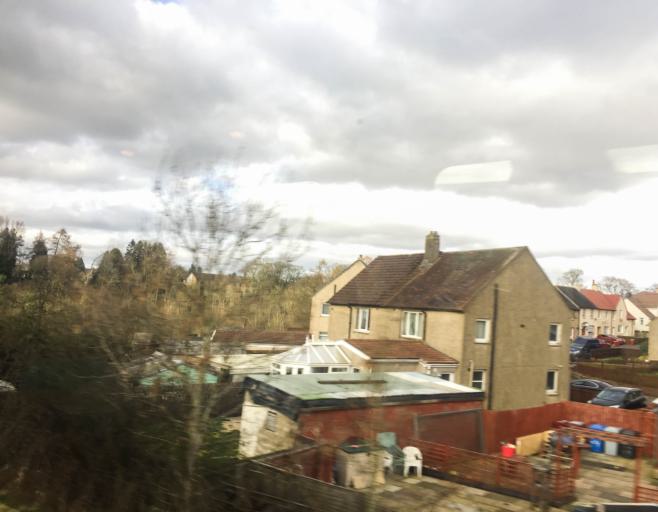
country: GB
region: Scotland
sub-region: South Lanarkshire
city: Carluke
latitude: 55.7293
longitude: -3.8459
